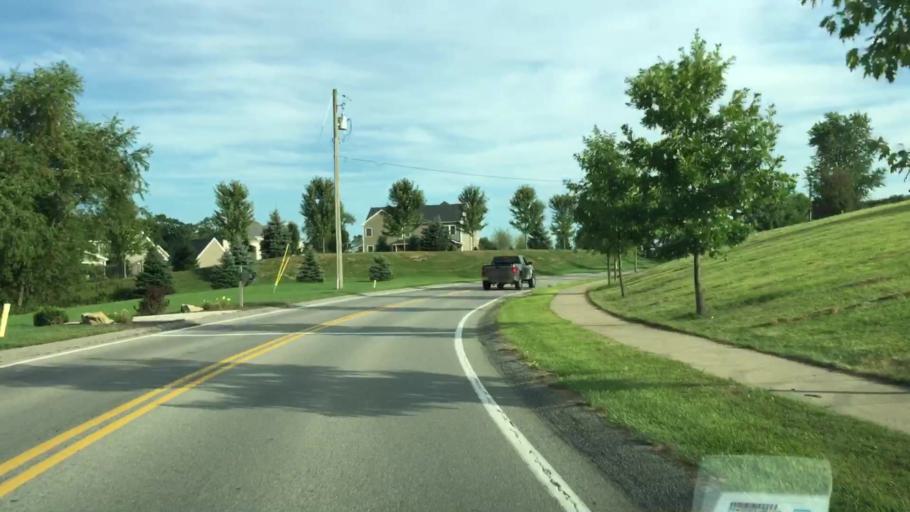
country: US
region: Pennsylvania
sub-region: Butler County
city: Fox Run
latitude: 40.7383
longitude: -80.0877
